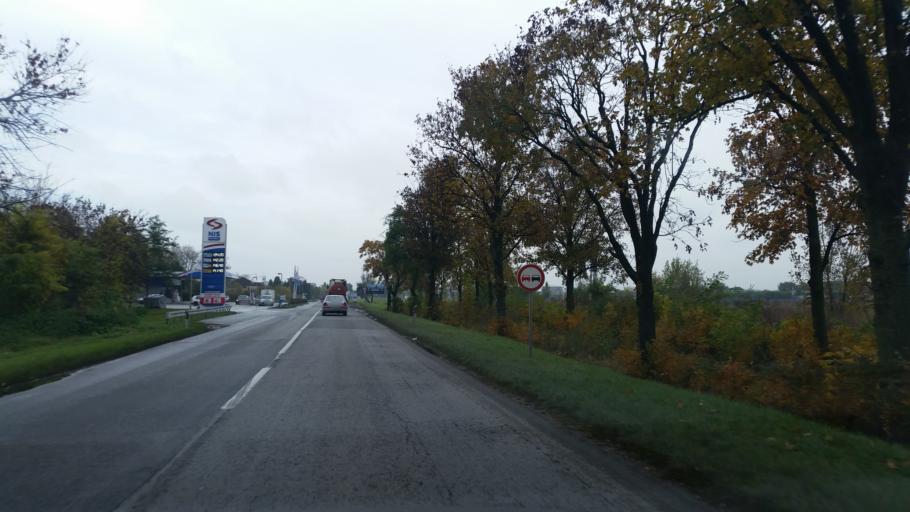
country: RS
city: Ecka
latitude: 45.3478
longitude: 20.4244
